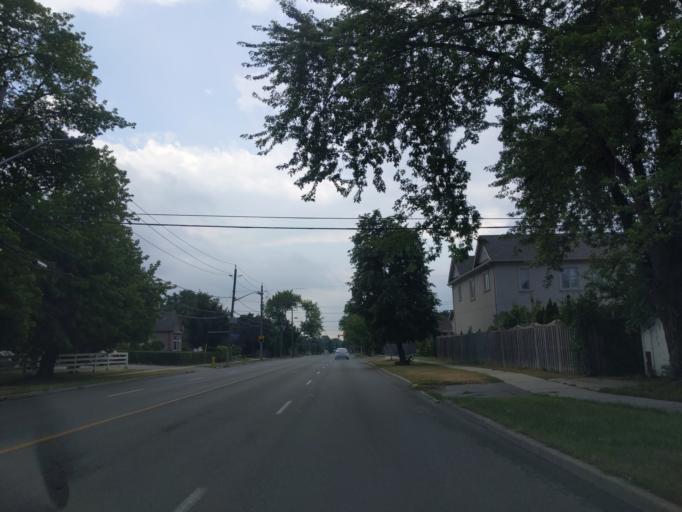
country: CA
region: Ontario
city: North York
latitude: 43.7974
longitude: -79.4137
